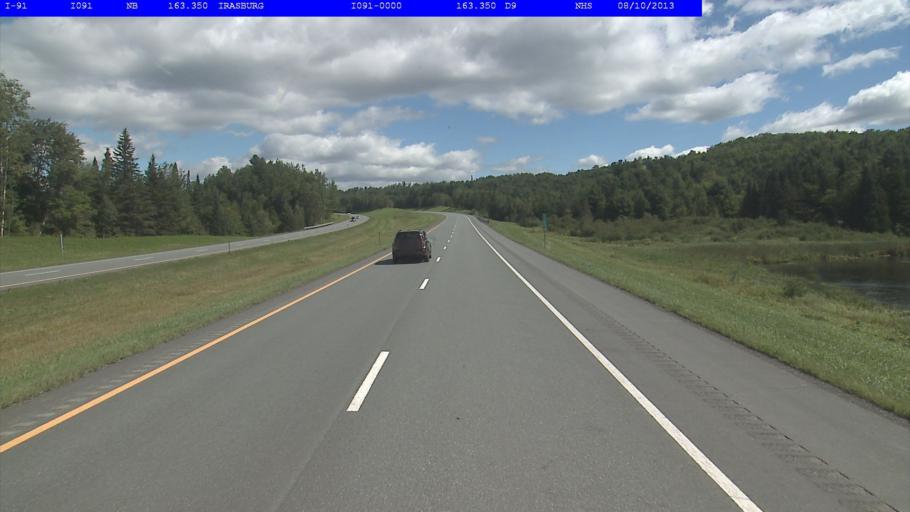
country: US
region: Vermont
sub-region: Orleans County
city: Newport
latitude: 44.8316
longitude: -72.1984
